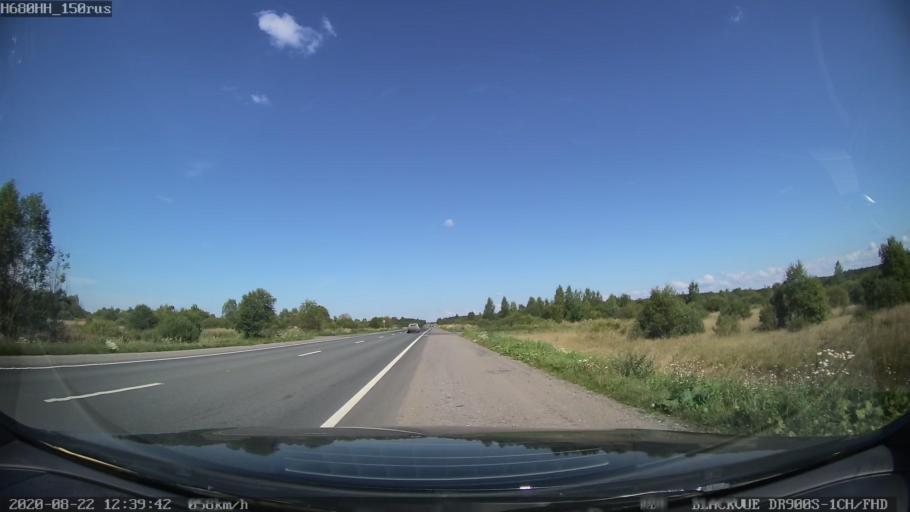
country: RU
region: Tverskaya
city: Rameshki
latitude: 57.3343
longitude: 36.0944
